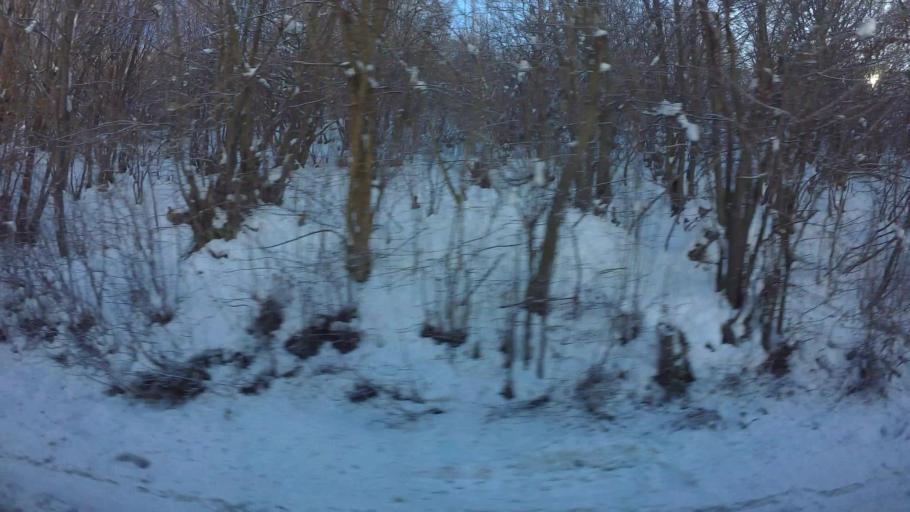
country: BA
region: Federation of Bosnia and Herzegovina
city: Kobilja Glava
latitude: 43.8895
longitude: 18.4169
